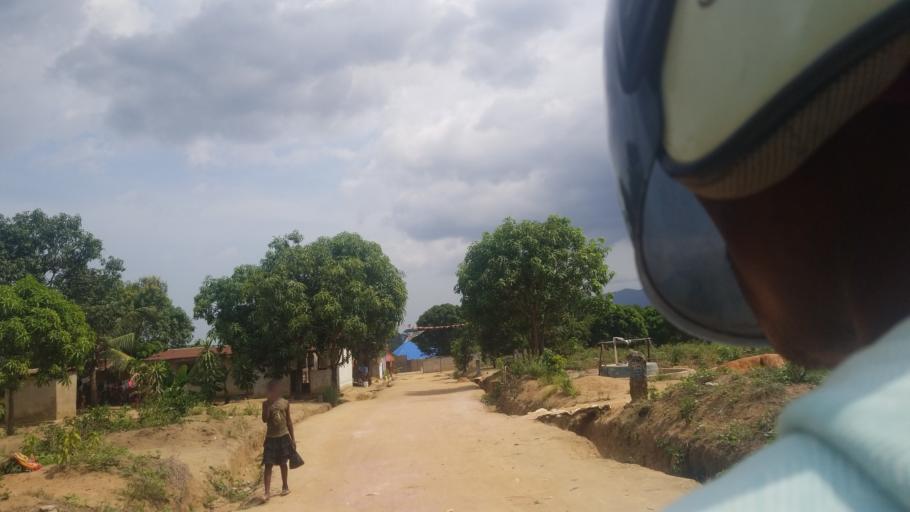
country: SL
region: Western Area
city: Waterloo
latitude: 8.3157
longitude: -13.0459
